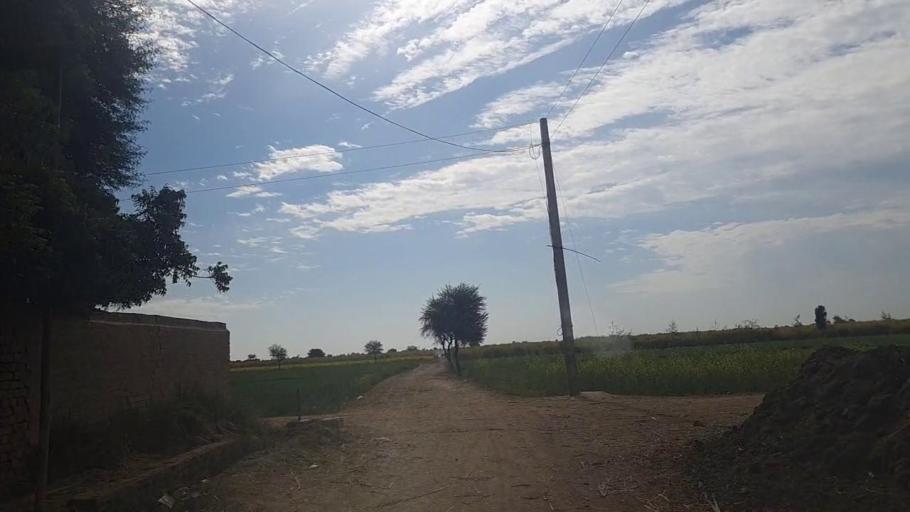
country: PK
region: Sindh
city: Sinjhoro
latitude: 26.1226
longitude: 68.8344
